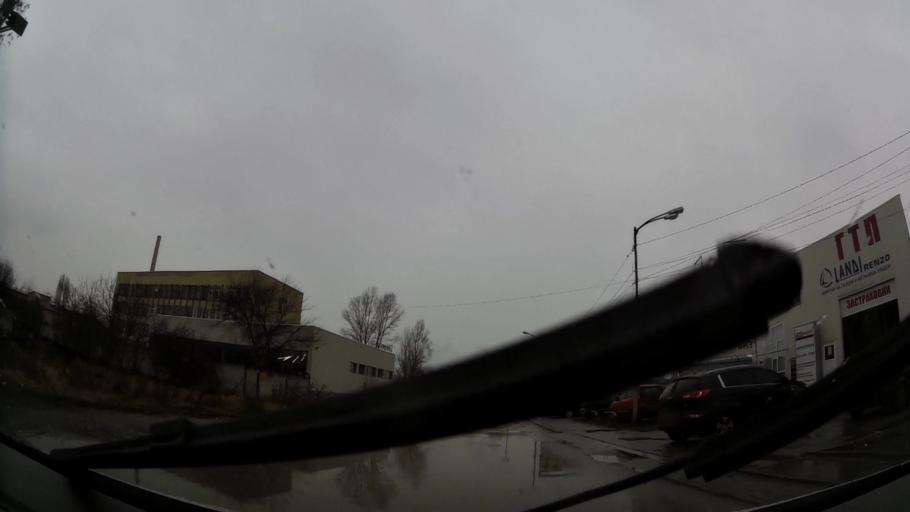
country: BG
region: Sofia-Capital
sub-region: Stolichna Obshtina
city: Sofia
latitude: 42.6615
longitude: 23.4200
